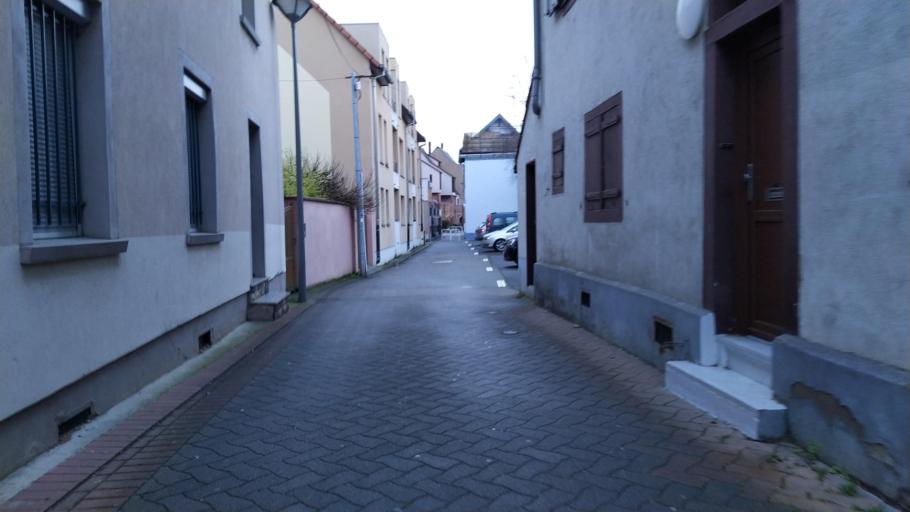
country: FR
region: Alsace
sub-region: Departement du Bas-Rhin
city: Schiltigheim
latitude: 48.6081
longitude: 7.7516
